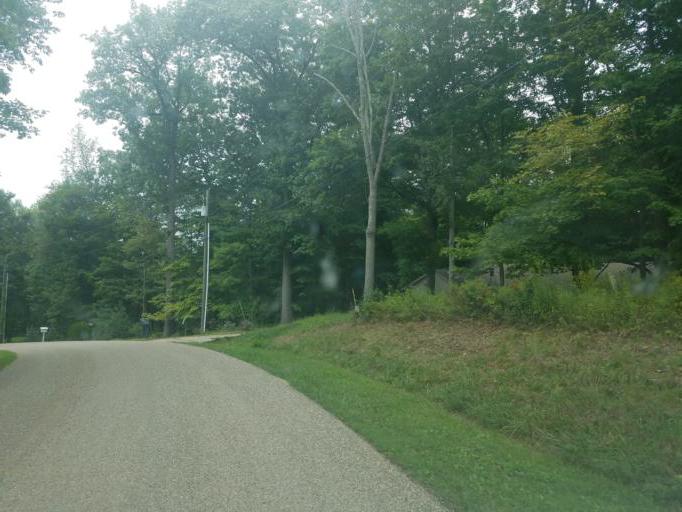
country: US
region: Ohio
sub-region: Knox County
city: Danville
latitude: 40.4559
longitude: -82.3338
